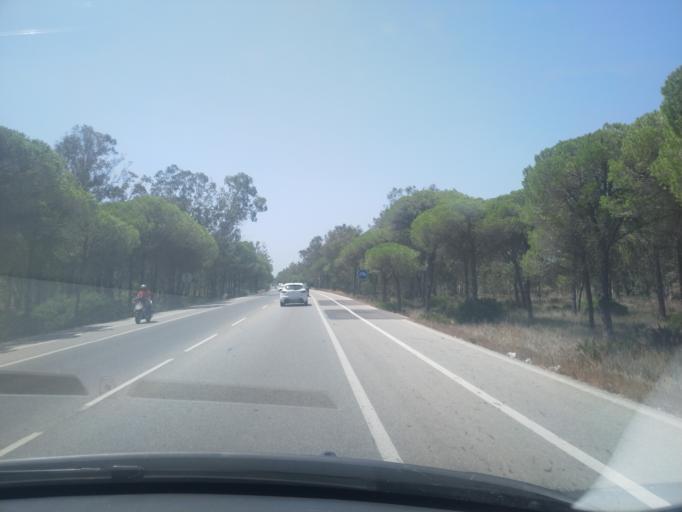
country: ES
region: Andalusia
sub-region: Provincia de Cadiz
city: Chiclana de la Frontera
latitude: 36.3908
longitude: -6.1243
